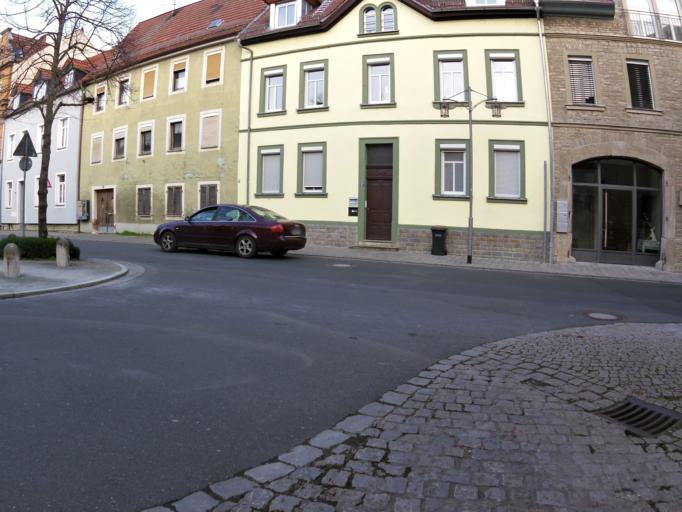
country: DE
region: Bavaria
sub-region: Regierungsbezirk Unterfranken
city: Kitzingen
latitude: 49.7360
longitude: 10.1644
